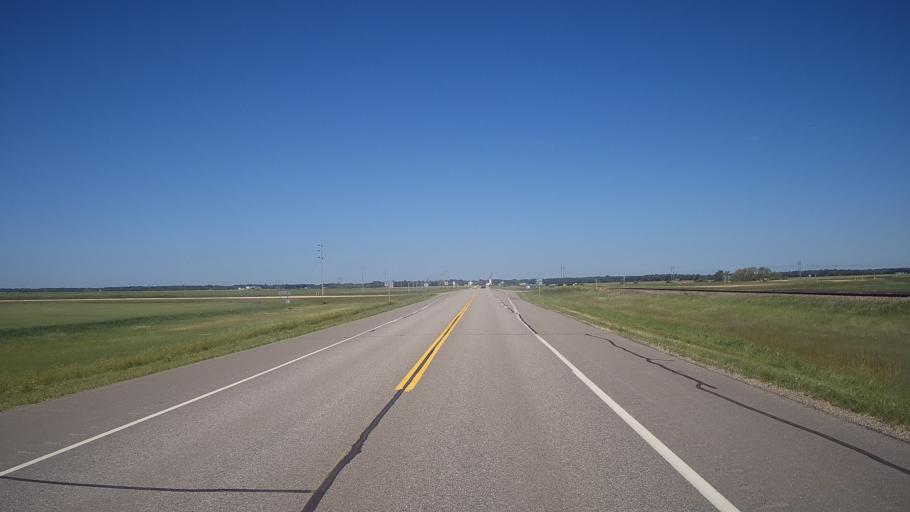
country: CA
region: Manitoba
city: Portage la Prairie
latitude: 50.1168
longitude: -98.5577
